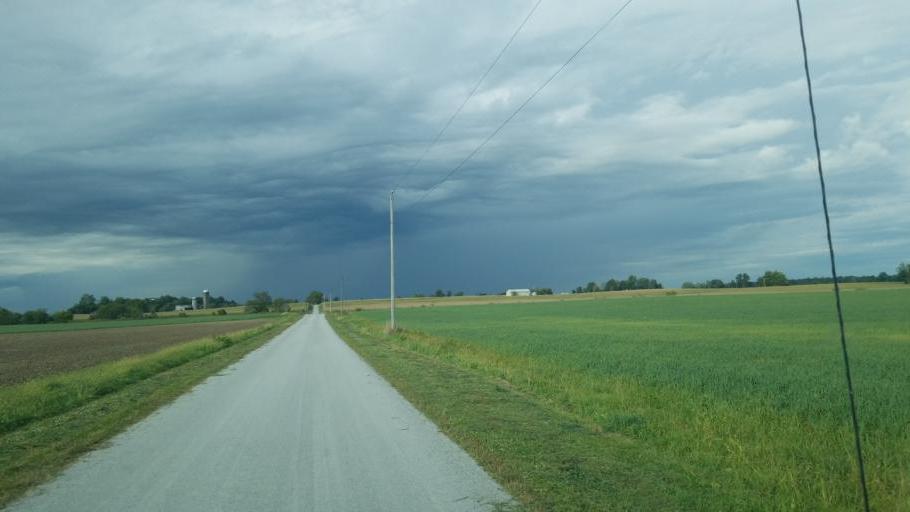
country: US
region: Ohio
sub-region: Hardin County
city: Forest
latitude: 40.8618
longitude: -83.4915
